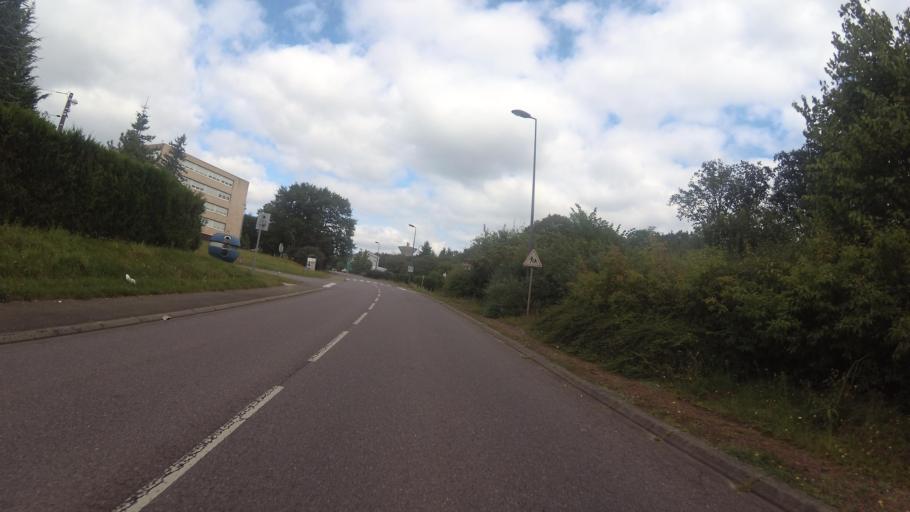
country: FR
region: Lorraine
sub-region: Departement de la Moselle
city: Creutzwald
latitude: 49.2082
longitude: 6.7136
